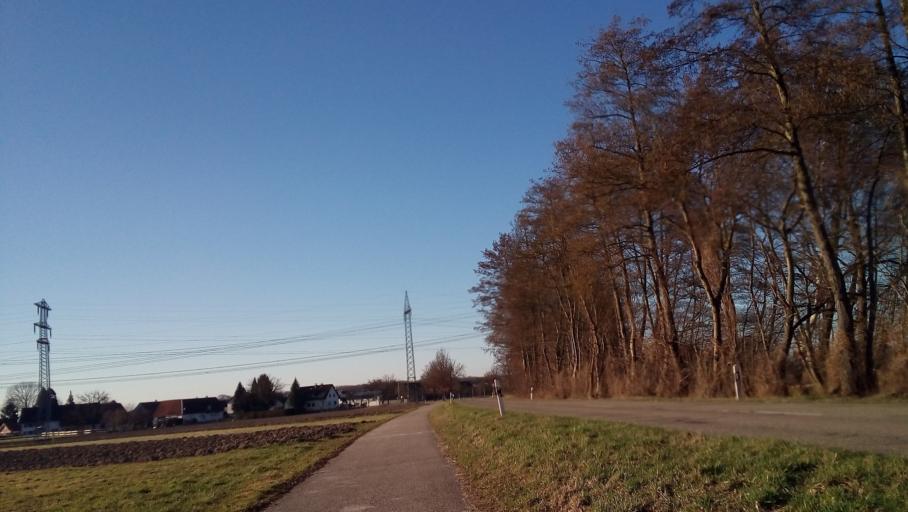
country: DE
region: Baden-Wuerttemberg
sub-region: Freiburg Region
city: Achern
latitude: 48.6464
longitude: 8.0511
